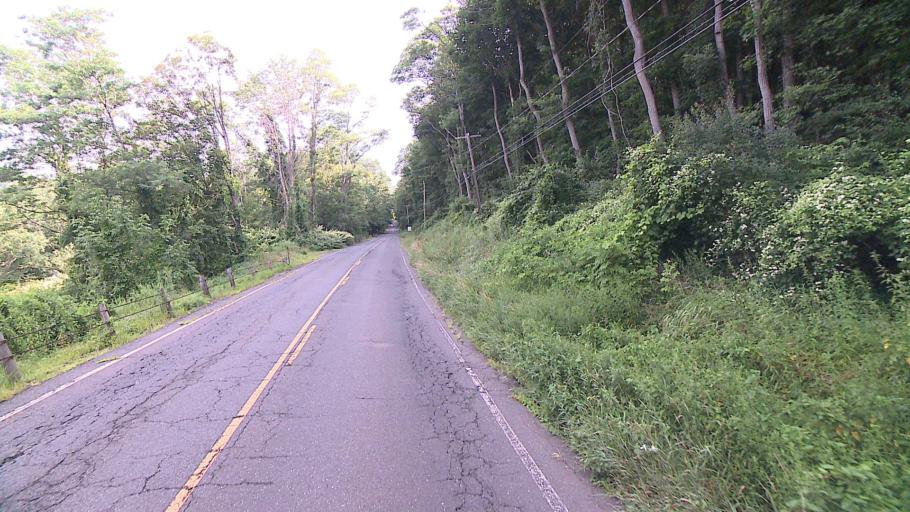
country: US
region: New York
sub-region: Putnam County
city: Putnam Lake
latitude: 41.5015
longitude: -73.5293
